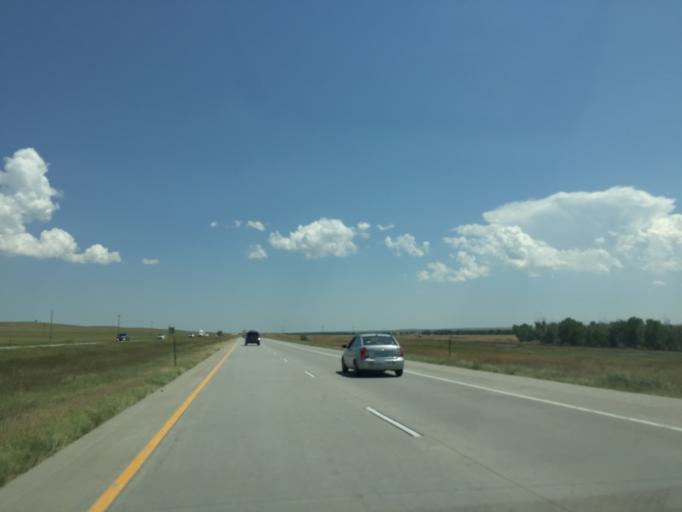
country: US
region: Colorado
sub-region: Lincoln County
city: Limon
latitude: 39.3014
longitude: -103.8133
